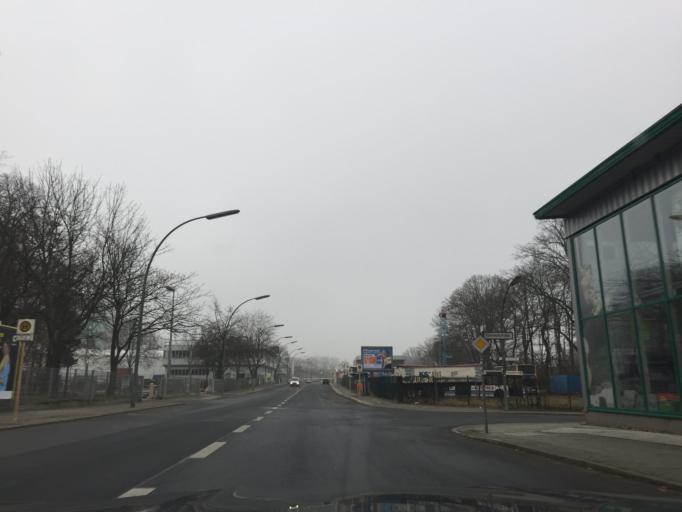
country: DE
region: Berlin
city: Haselhorst
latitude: 52.5295
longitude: 13.2326
